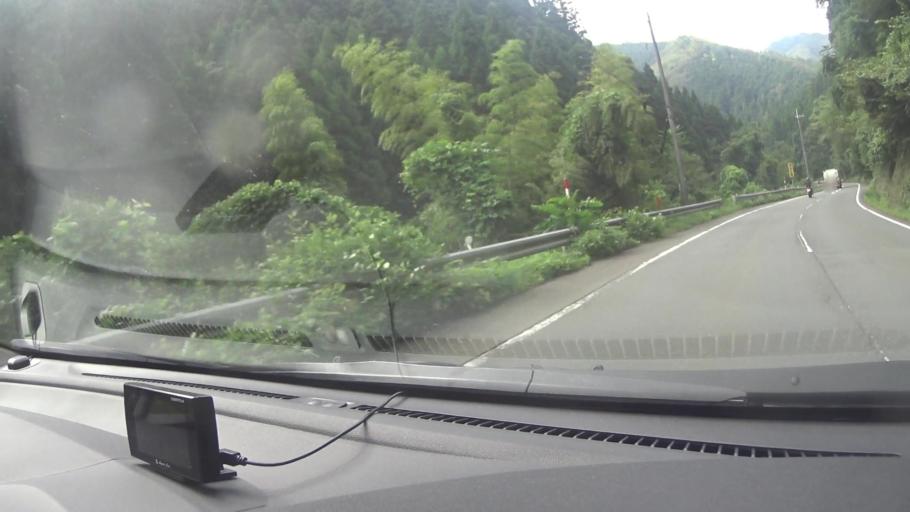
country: JP
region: Kyoto
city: Ayabe
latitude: 35.2422
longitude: 135.3052
